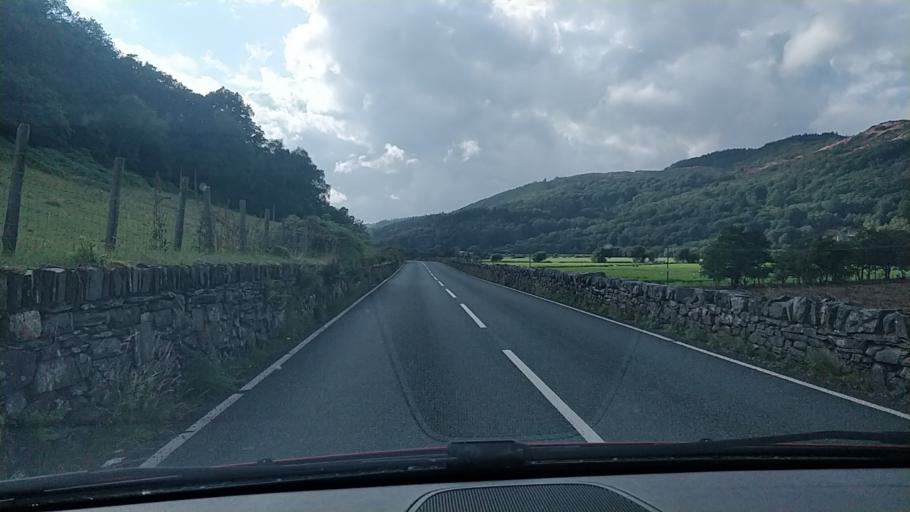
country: GB
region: Wales
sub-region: Gwynedd
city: Maentwrog
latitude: 52.9367
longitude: -4.0066
